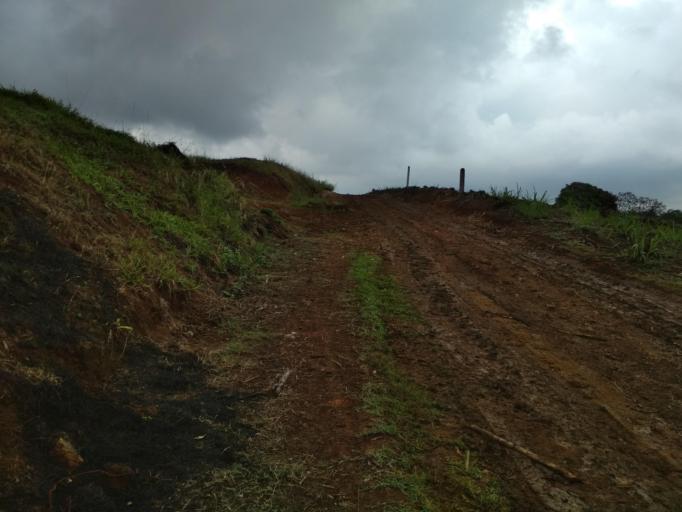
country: MX
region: Veracruz
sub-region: Cordoba
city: San Jose de Tapia
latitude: 18.8486
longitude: -96.9621
